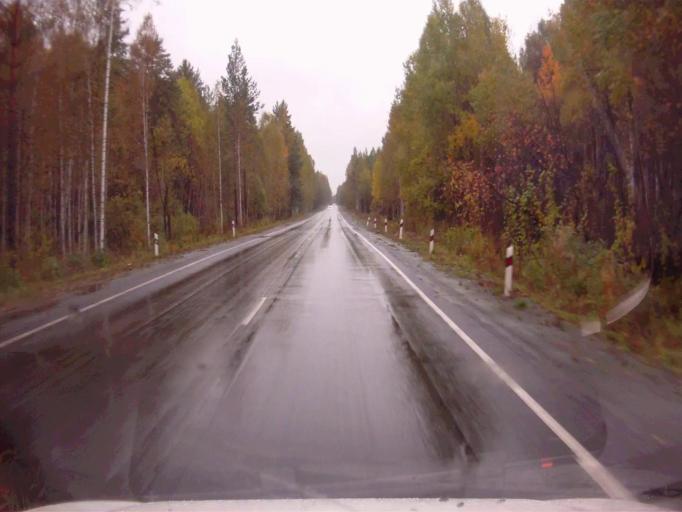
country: RU
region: Chelyabinsk
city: Tayginka
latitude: 55.5799
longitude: 60.6418
